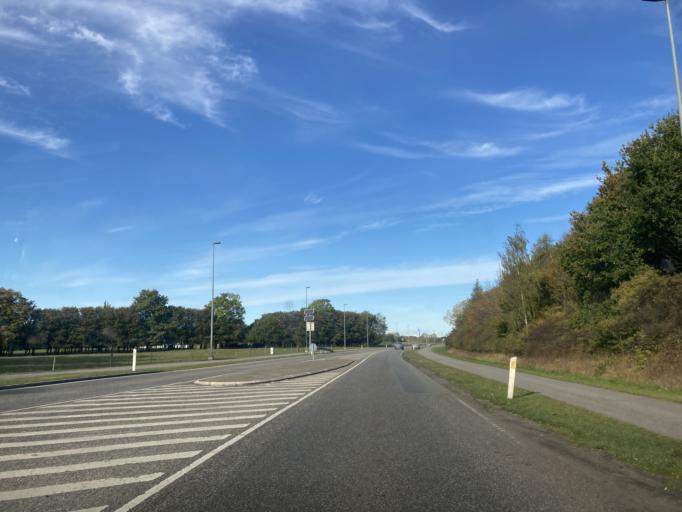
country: DK
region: Capital Region
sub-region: Vallensbaek Kommune
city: Vallensbaek
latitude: 55.6330
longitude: 12.3766
